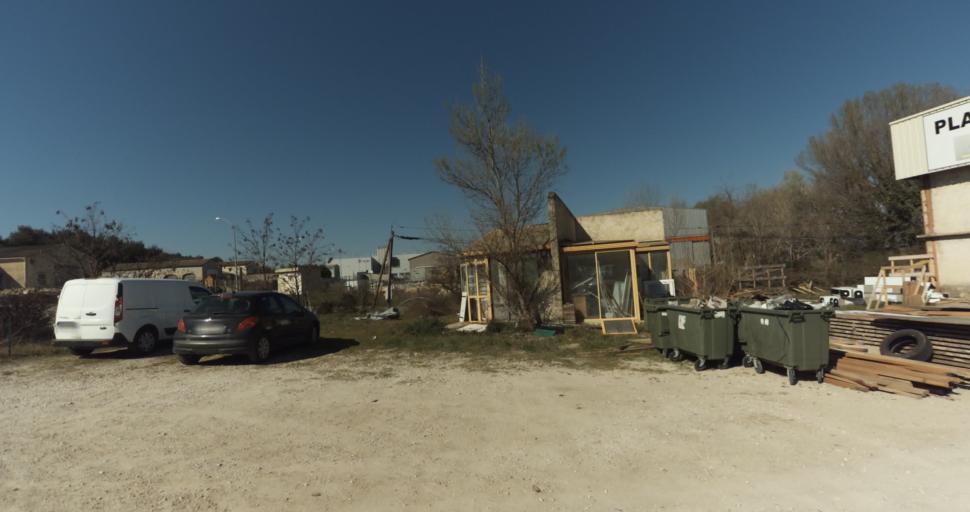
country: FR
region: Provence-Alpes-Cote d'Azur
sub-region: Departement des Bouches-du-Rhone
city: Charleval
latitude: 43.7229
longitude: 5.2757
